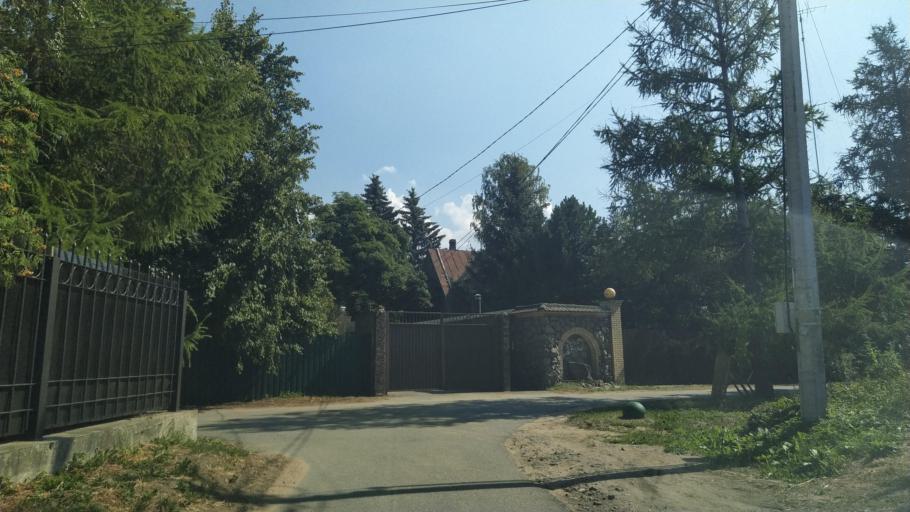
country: RU
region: St.-Petersburg
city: Lakhtinskiy
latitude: 59.9893
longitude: 30.1569
